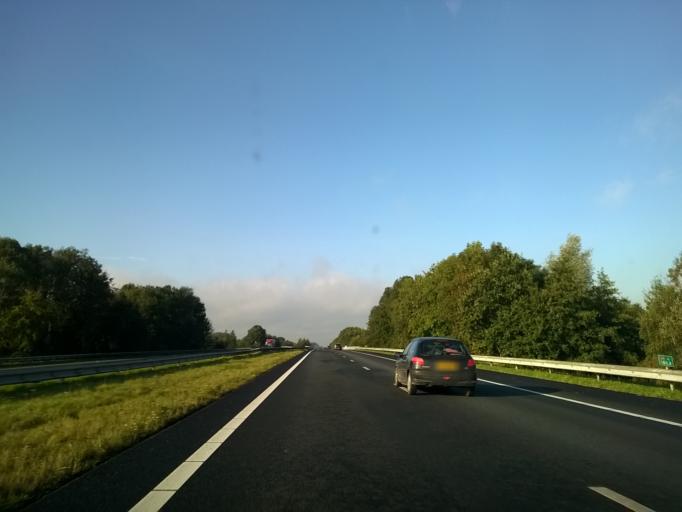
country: NL
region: Groningen
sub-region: Gemeente Leek
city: Leek
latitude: 53.1717
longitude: 6.3358
